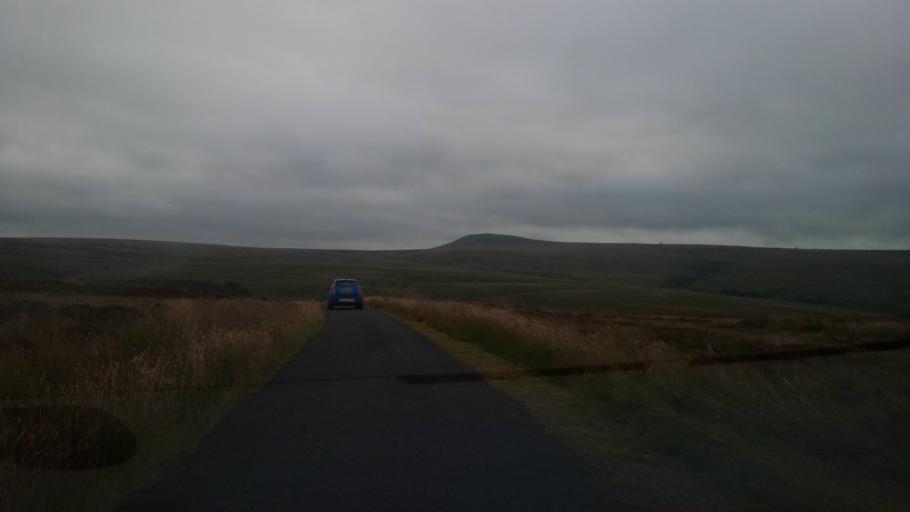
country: GB
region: Scotland
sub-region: Dumfries and Galloway
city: Langholm
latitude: 55.1687
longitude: -2.9436
